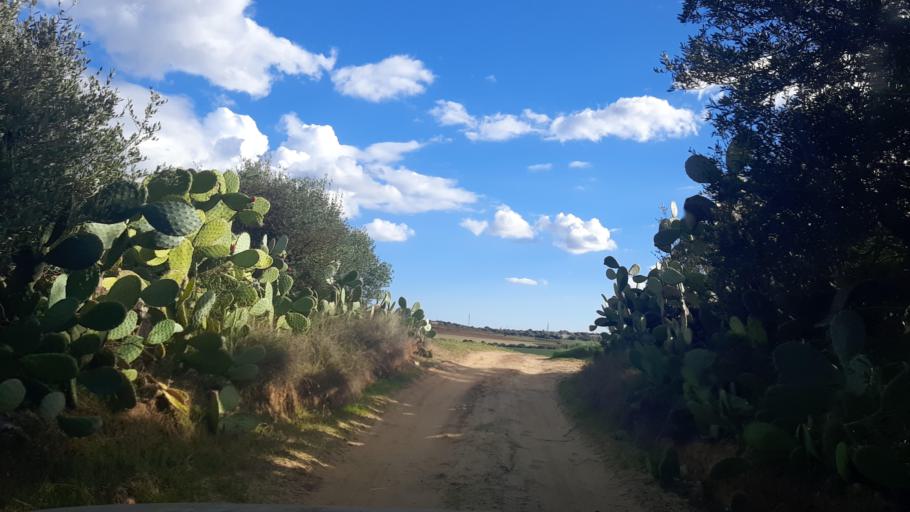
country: TN
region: Nabul
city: Bu `Urqub
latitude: 36.4510
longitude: 10.5008
